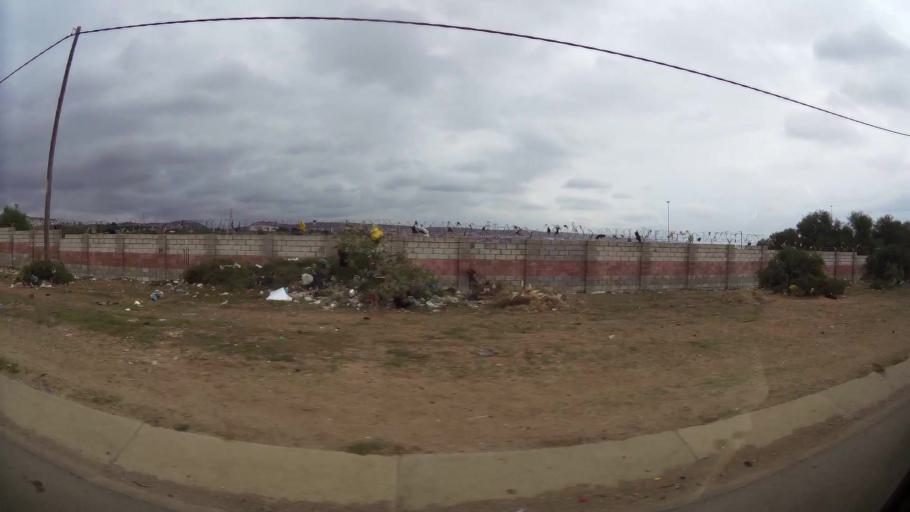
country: ZA
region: Eastern Cape
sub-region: Nelson Mandela Bay Metropolitan Municipality
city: Port Elizabeth
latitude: -33.8893
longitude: 25.5549
